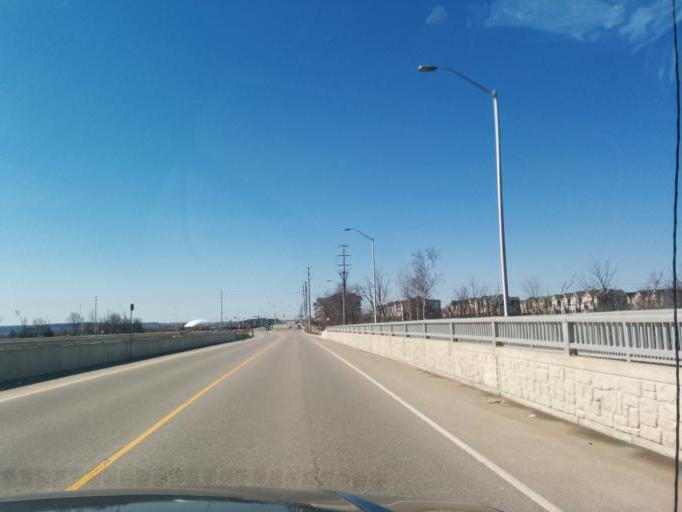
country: CA
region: Ontario
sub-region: Halton
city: Milton
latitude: 43.4986
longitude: -79.8460
